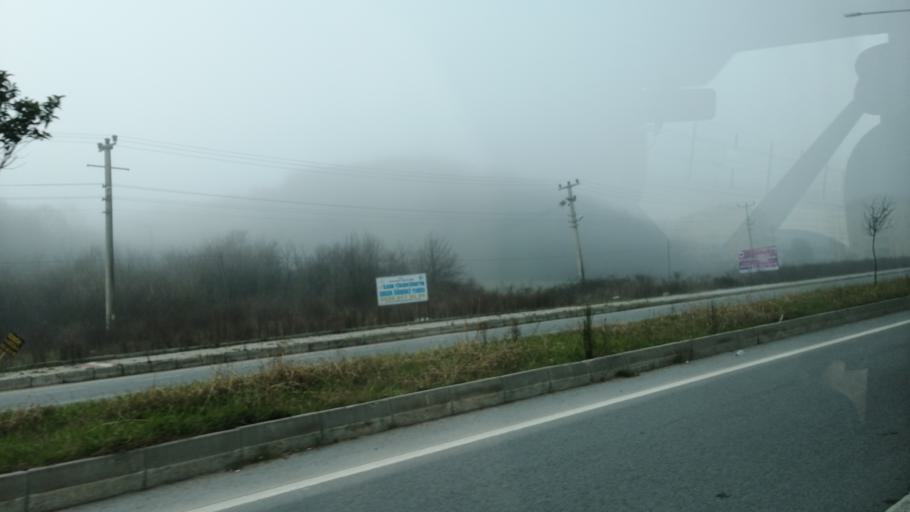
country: TR
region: Yalova
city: Kadikoy
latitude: 40.6500
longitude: 29.2263
